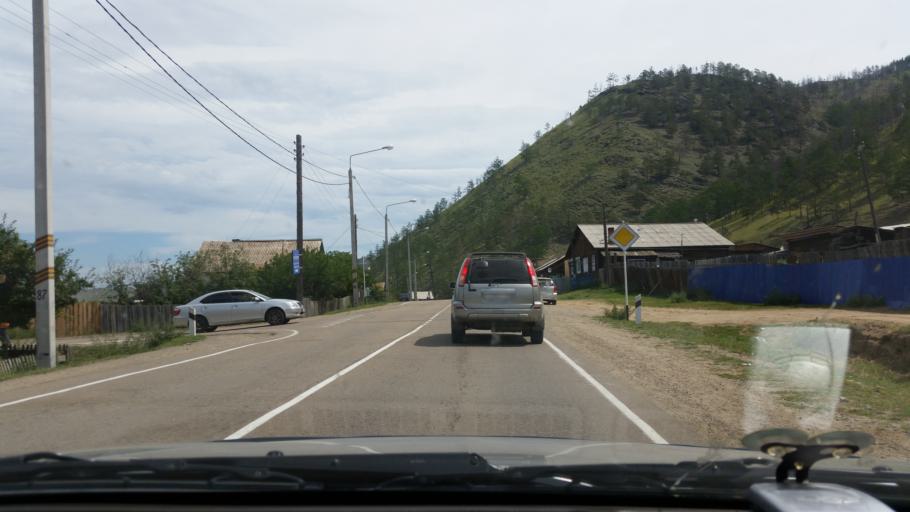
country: RU
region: Irkutsk
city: Yelantsy
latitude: 52.7975
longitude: 106.4119
